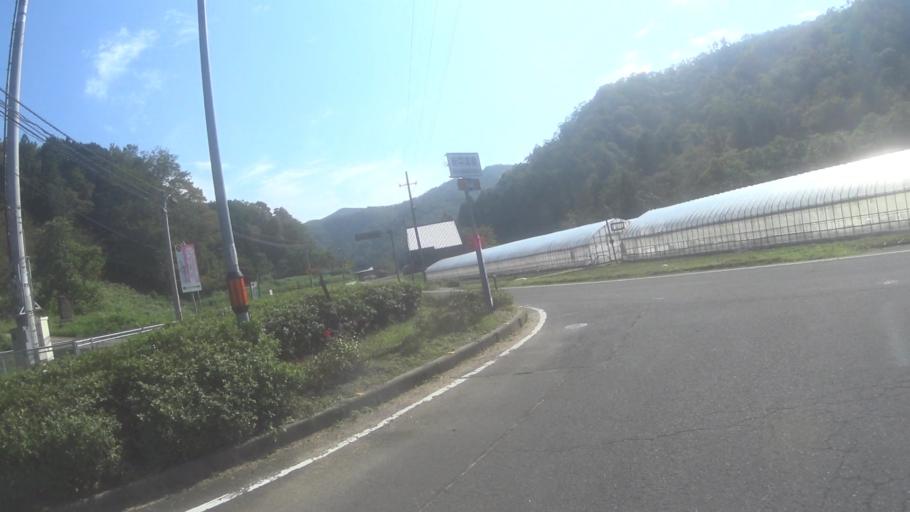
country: JP
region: Kyoto
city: Miyazu
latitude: 35.6921
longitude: 135.1496
